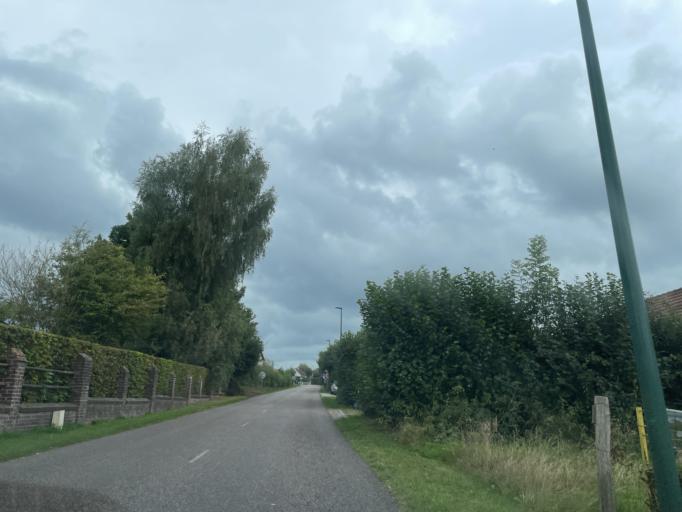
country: FR
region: Haute-Normandie
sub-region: Departement de la Seine-Maritime
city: Neufchatel-en-Bray
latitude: 49.6786
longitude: 1.4305
